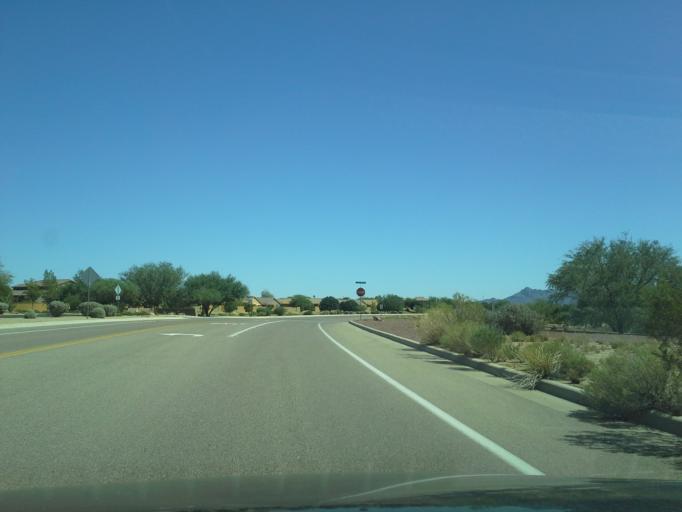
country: US
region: Arizona
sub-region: Pima County
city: Marana
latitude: 32.4655
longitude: -111.2137
